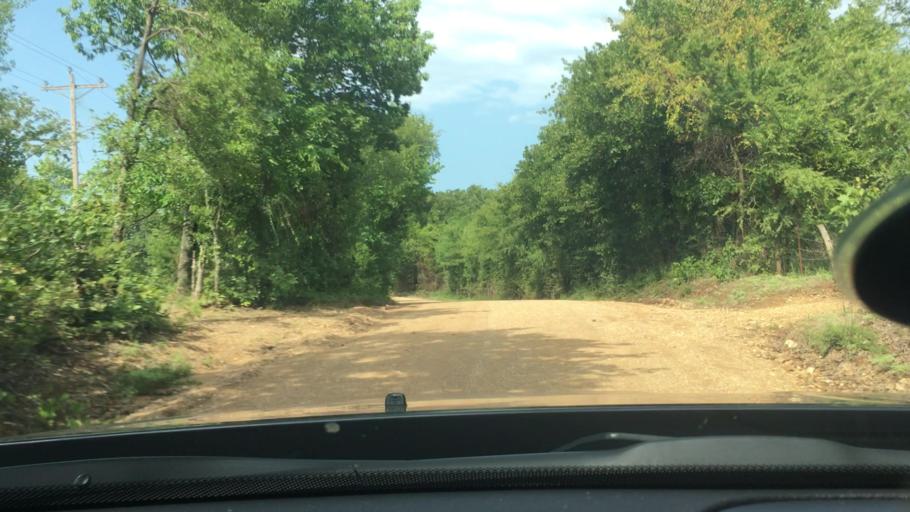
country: US
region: Oklahoma
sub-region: Atoka County
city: Atoka
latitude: 34.4451
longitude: -96.0523
